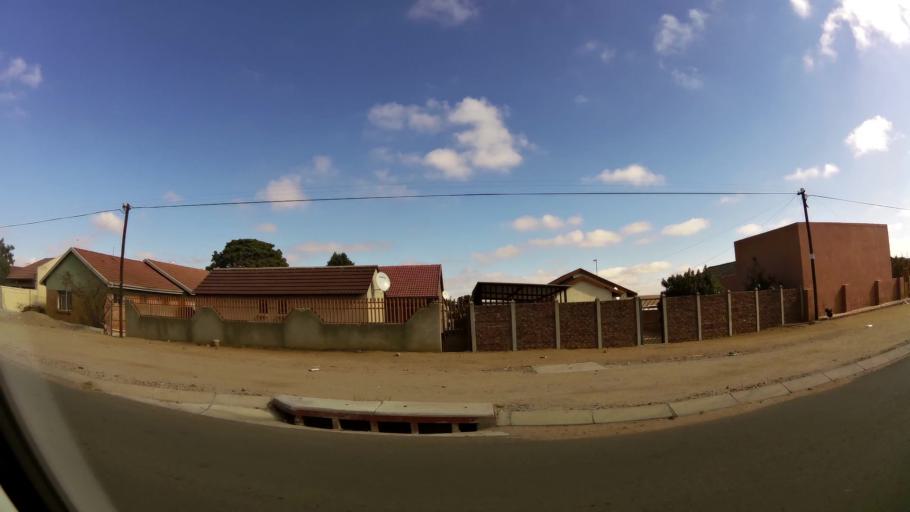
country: ZA
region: Limpopo
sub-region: Capricorn District Municipality
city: Polokwane
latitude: -23.8552
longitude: 29.3768
